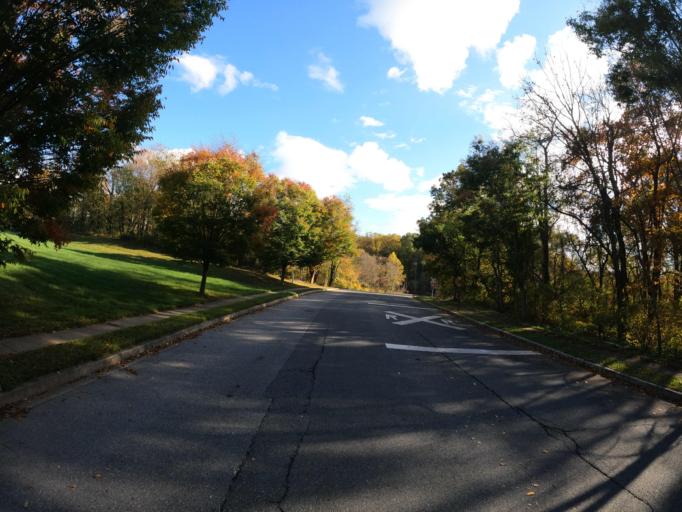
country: US
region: Maryland
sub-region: Carroll County
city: Mount Airy
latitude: 39.3672
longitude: -77.1760
